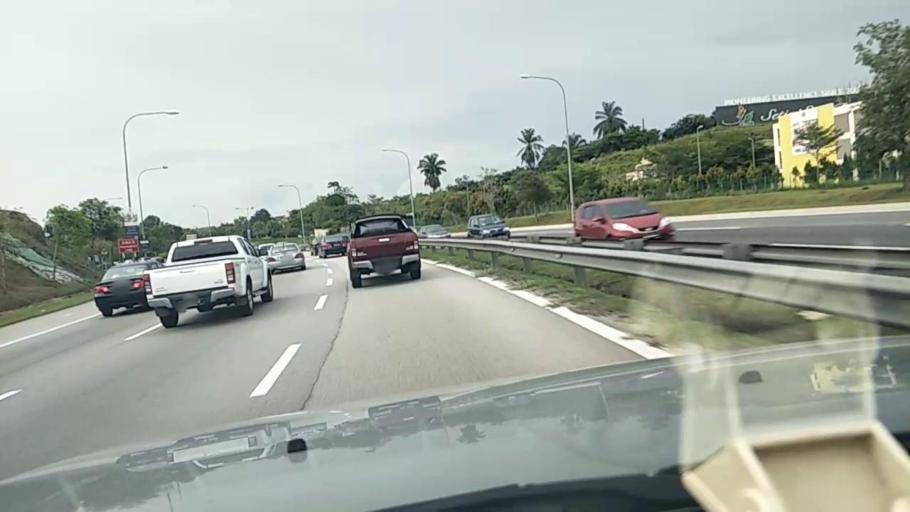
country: MY
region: Selangor
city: Shah Alam
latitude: 3.0972
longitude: 101.4826
